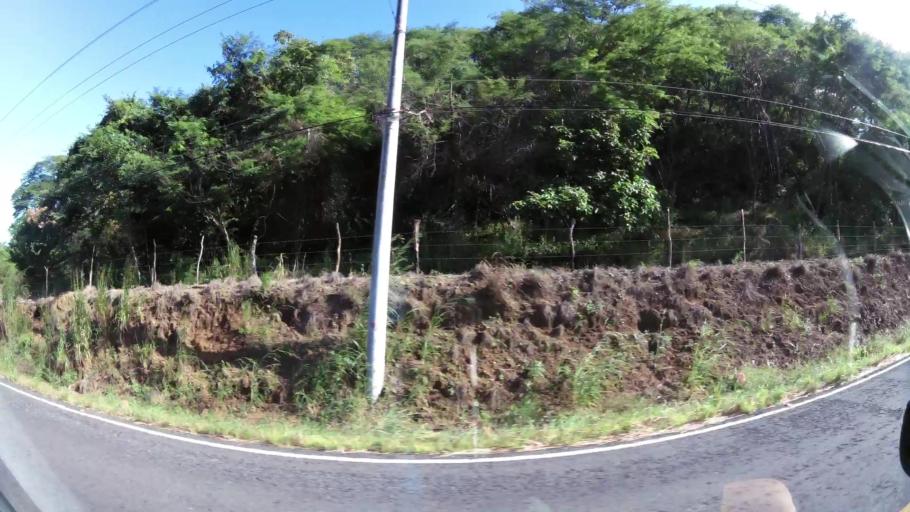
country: CR
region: Guanacaste
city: Sardinal
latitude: 10.5745
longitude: -85.6299
